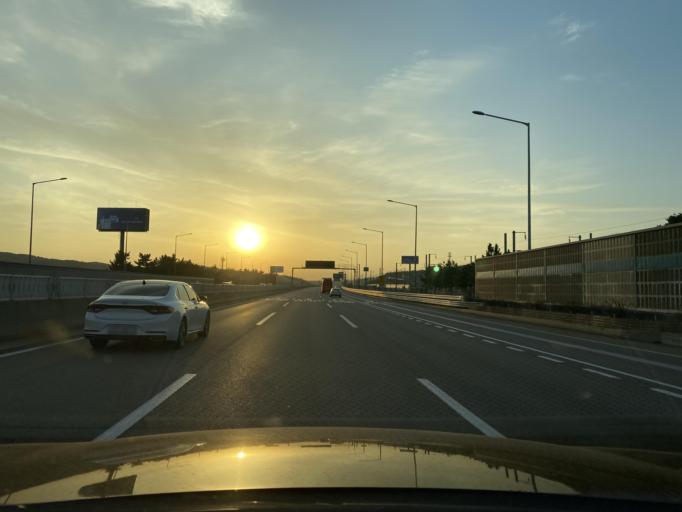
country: KR
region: Incheon
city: Incheon
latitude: 37.5102
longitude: 126.5212
